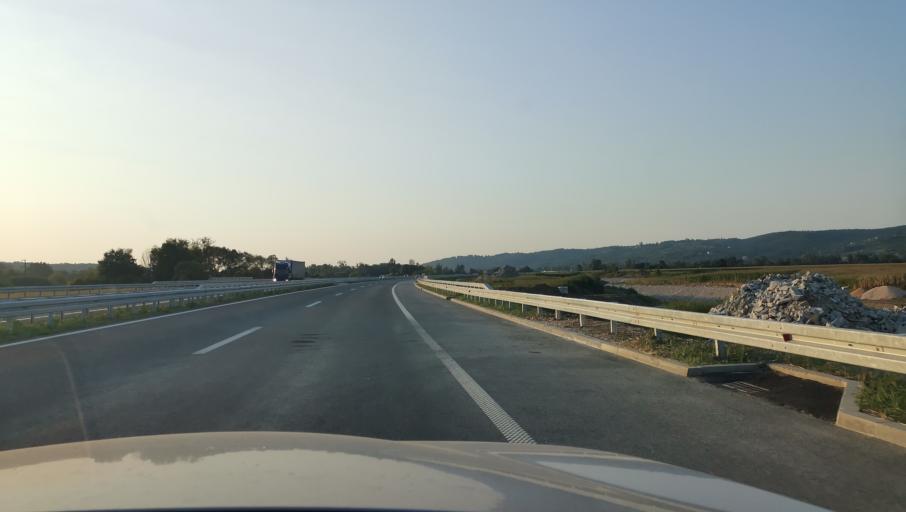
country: RS
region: Central Serbia
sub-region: Kolubarski Okrug
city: Lajkovac
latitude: 44.3158
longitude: 20.2153
